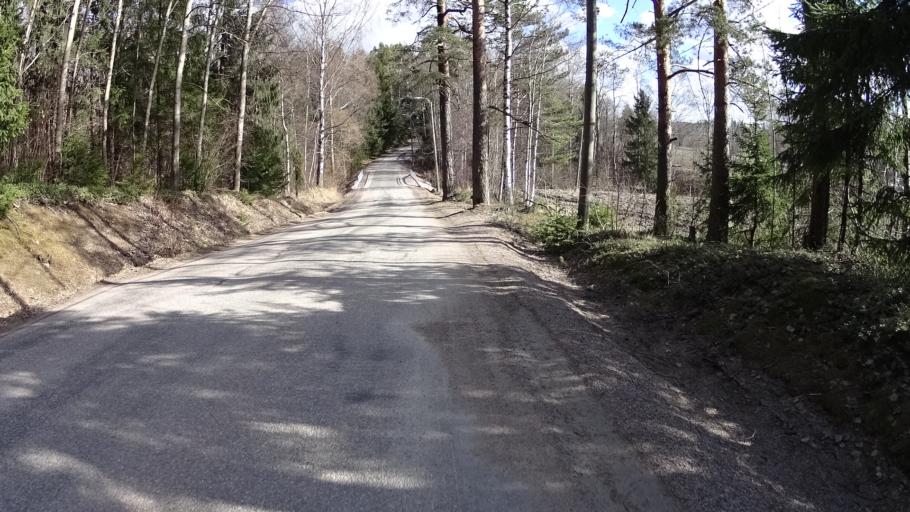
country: FI
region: Uusimaa
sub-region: Helsinki
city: Kilo
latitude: 60.2716
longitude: 24.7682
